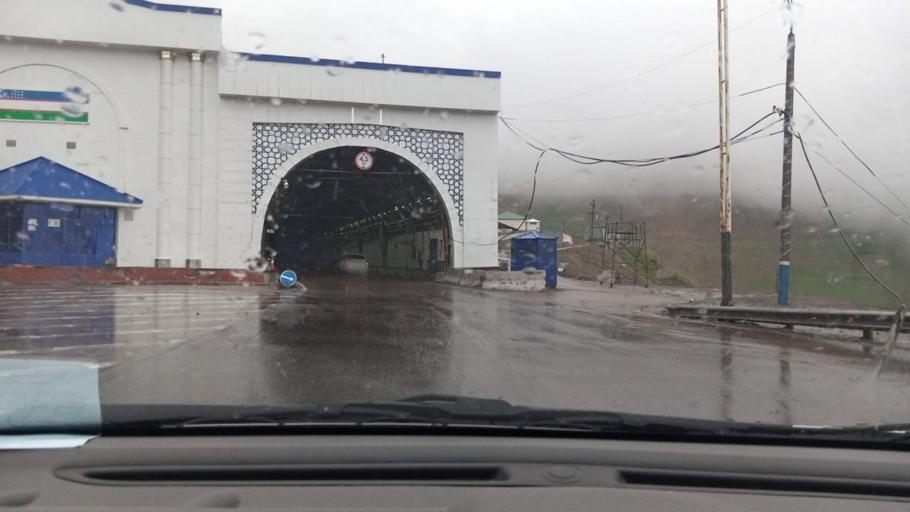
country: UZ
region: Toshkent
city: Angren
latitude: 41.1029
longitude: 70.5140
